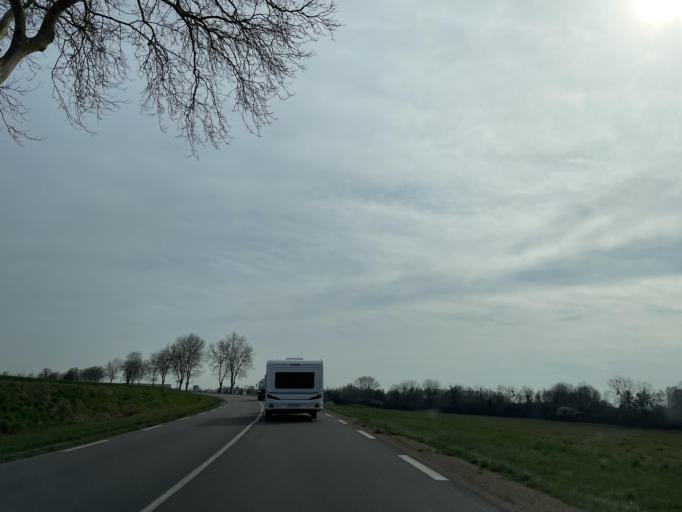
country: FR
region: Champagne-Ardenne
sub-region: Departement de l'Aube
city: Romilly-sur-Seine
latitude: 48.5081
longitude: 3.6916
